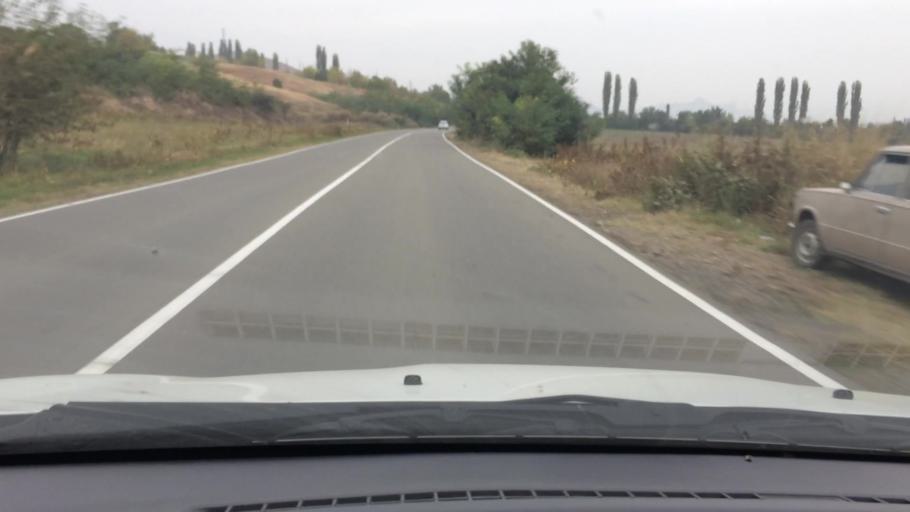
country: AM
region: Tavush
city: Bagratashen
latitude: 41.2727
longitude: 44.7906
